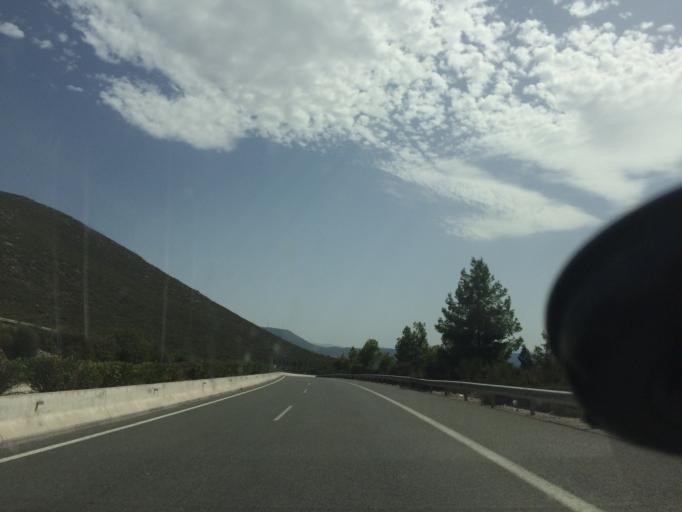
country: GR
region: Central Greece
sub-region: Nomos Fthiotidos
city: Martinon
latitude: 38.5427
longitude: 23.1679
